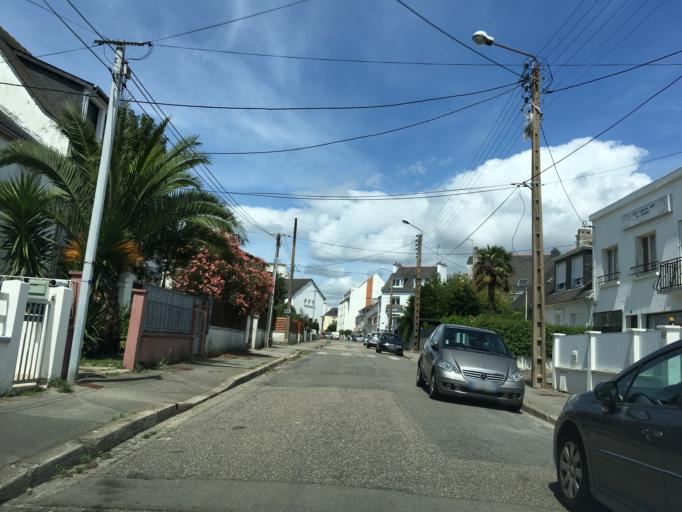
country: FR
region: Brittany
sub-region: Departement du Morbihan
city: Lorient
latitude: 47.7380
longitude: -3.3723
